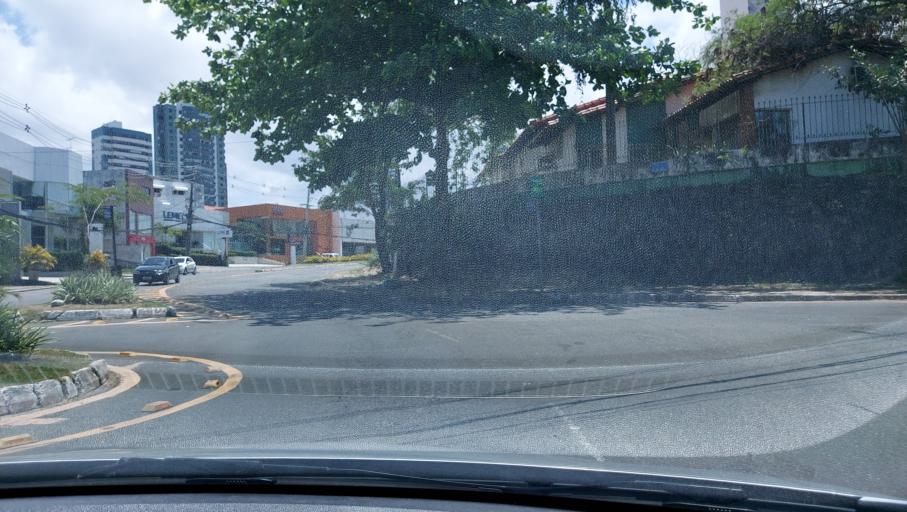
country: BR
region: Bahia
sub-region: Salvador
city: Salvador
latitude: -12.9836
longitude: -38.4581
